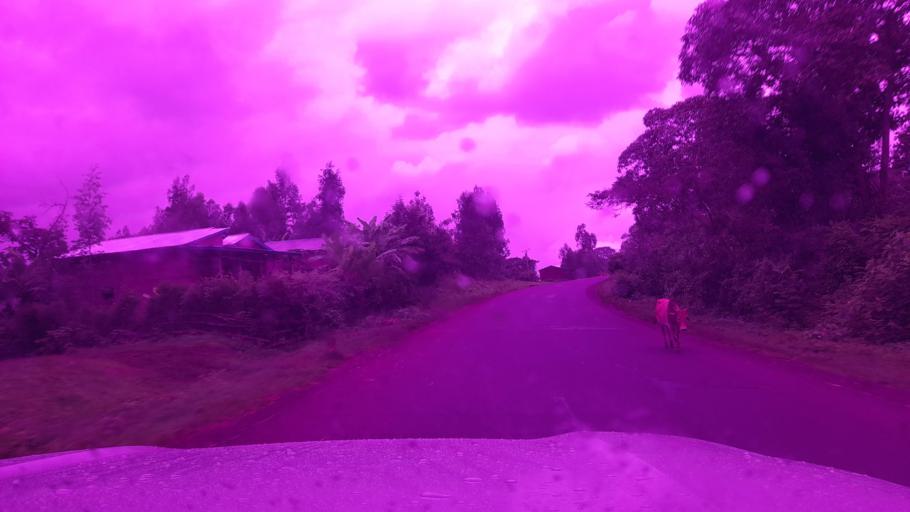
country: ET
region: Oromiya
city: Jima
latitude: 7.7086
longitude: 37.0526
